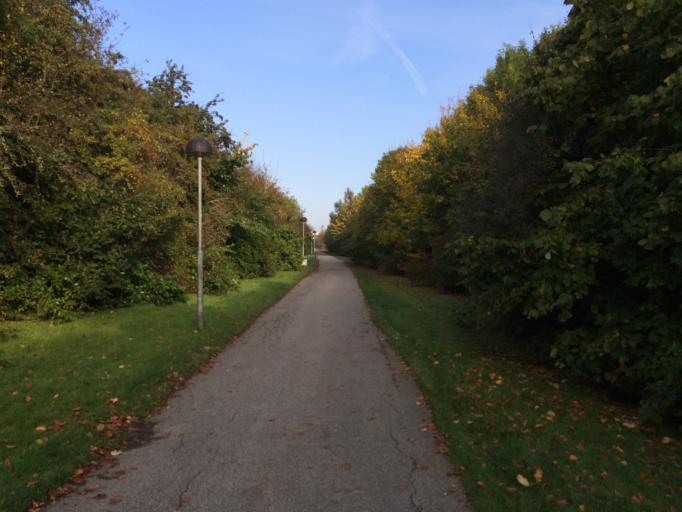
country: SE
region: Skane
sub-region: Lunds Kommun
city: Lund
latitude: 55.7070
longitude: 13.2416
